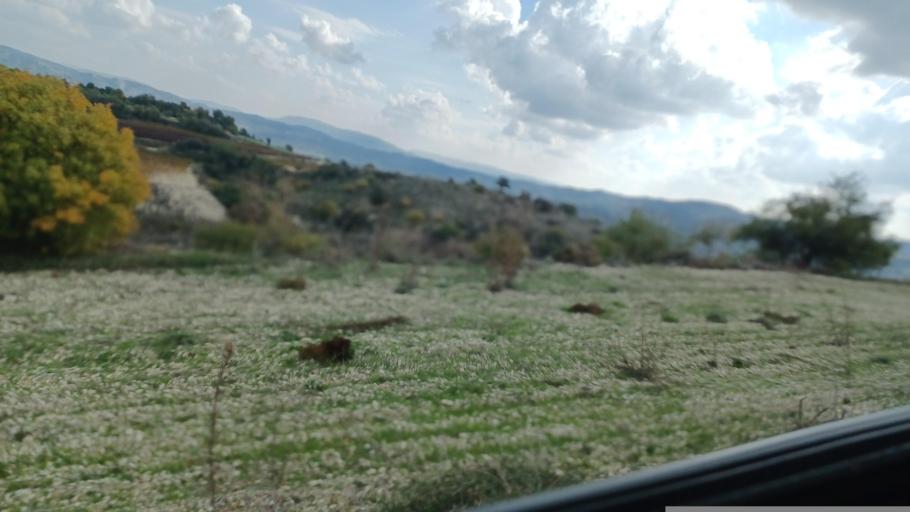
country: CY
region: Pafos
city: Mesogi
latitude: 34.8320
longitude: 32.5244
